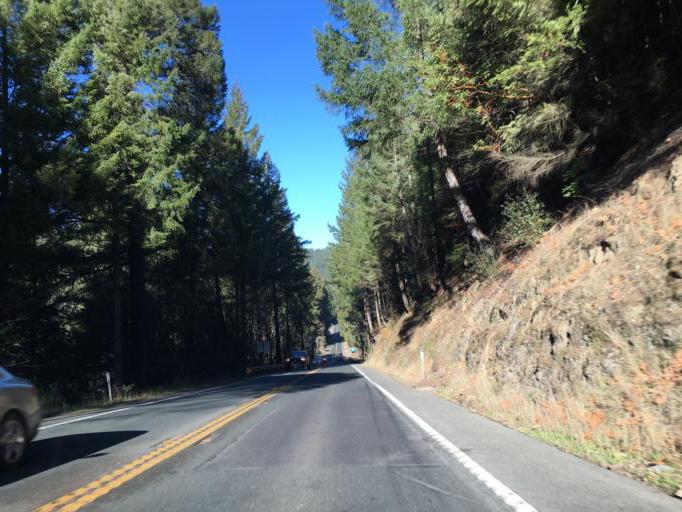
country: US
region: California
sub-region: Mendocino County
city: Brooktrails
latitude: 39.4781
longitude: -123.3635
